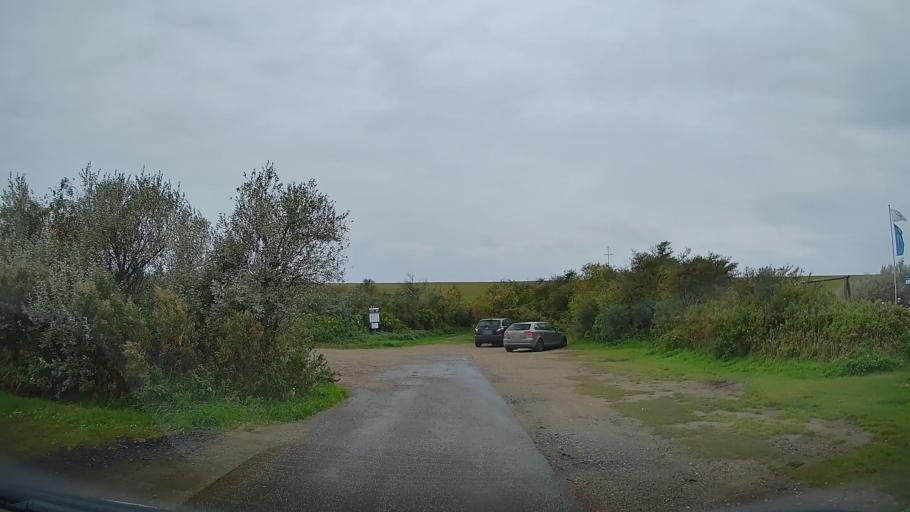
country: DE
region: Schleswig-Holstein
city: Friedrichsgabekoog
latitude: 54.1101
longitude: 8.9423
